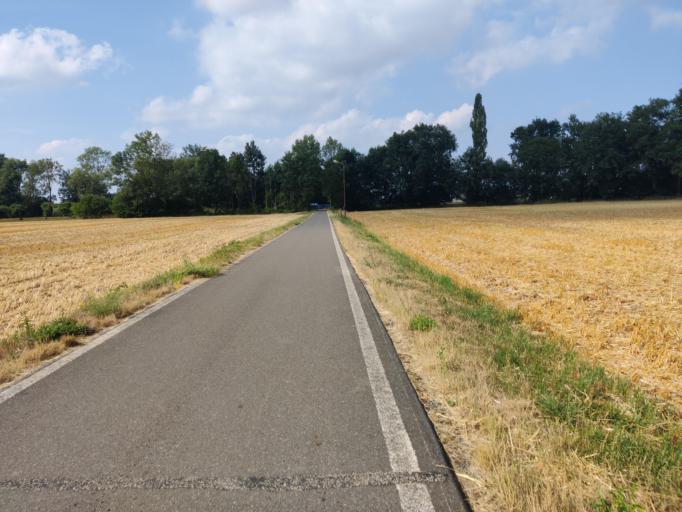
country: DE
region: Thuringia
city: Fockendorf
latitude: 51.0455
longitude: 12.4571
